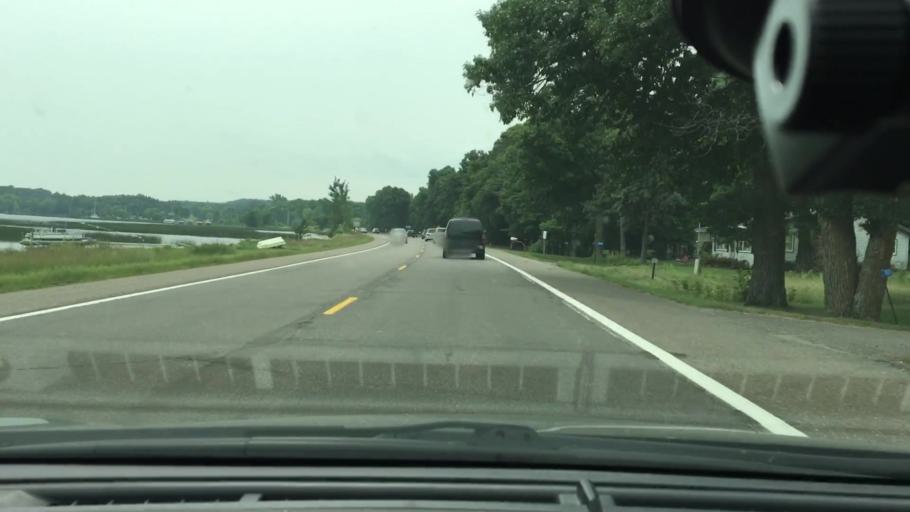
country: US
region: Minnesota
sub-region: Mille Lacs County
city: Vineland
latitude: 46.2581
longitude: -93.8232
